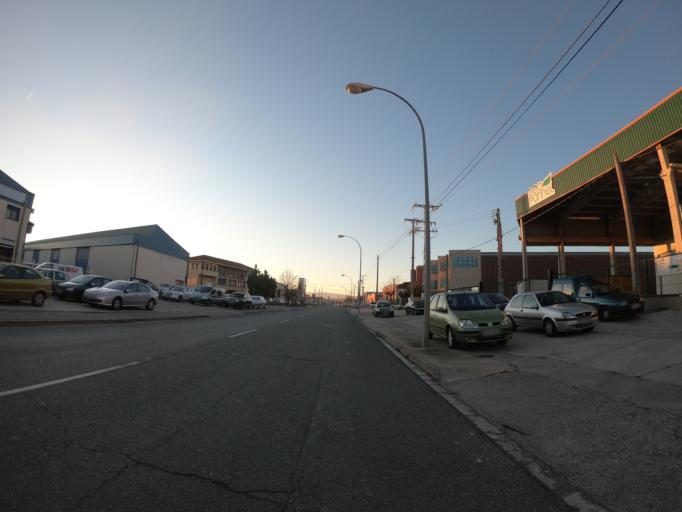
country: ES
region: Basque Country
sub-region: Provincia de Alava
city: Oyon
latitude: 42.4823
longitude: -2.4198
